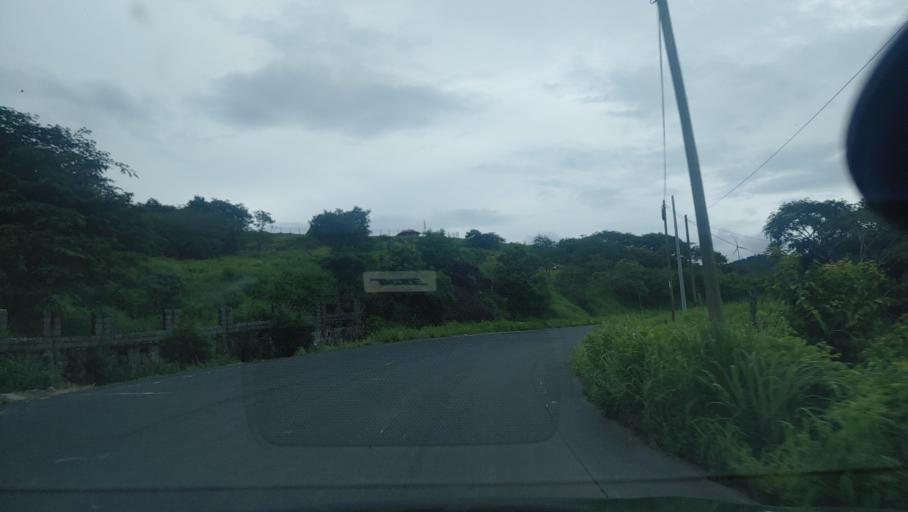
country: HN
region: Choluteca
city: Corpus
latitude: 13.3599
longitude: -86.9818
